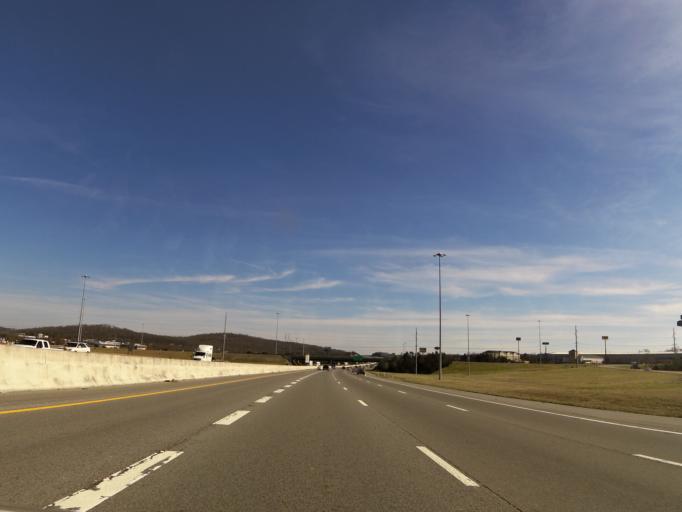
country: US
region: Tennessee
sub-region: Rutherford County
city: La Vergne
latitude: 35.9782
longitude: -86.5744
